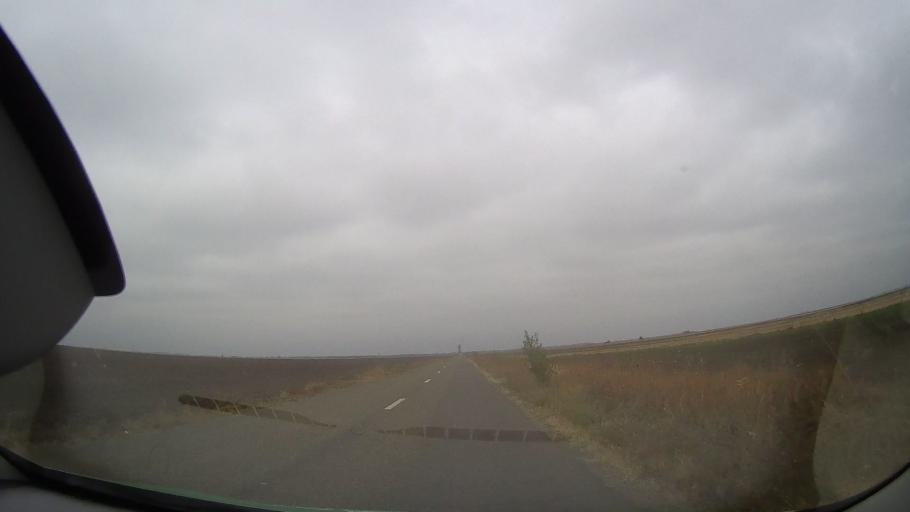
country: RO
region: Buzau
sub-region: Comuna Bradeanu
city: Bradeanu
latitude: 44.8965
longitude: 26.8730
